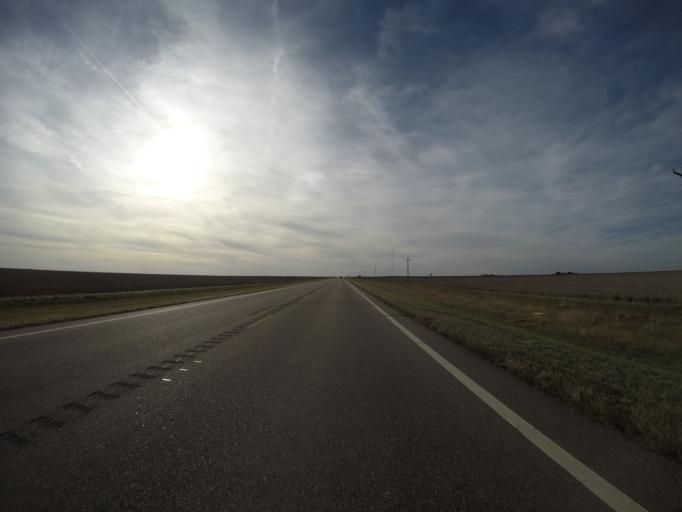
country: US
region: Kansas
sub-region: Cheyenne County
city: Saint Francis
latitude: 39.7567
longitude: -101.6784
